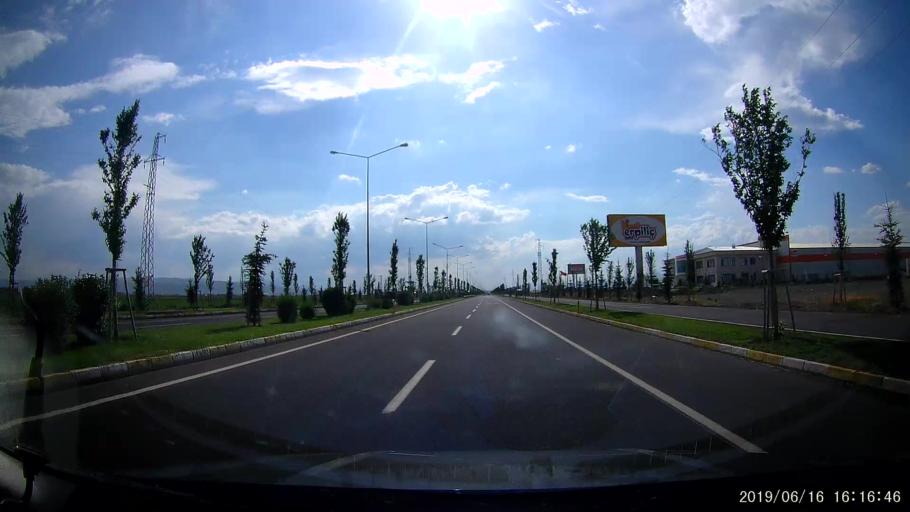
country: TR
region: Erzurum
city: Erzurum
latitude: 39.9632
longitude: 41.2014
